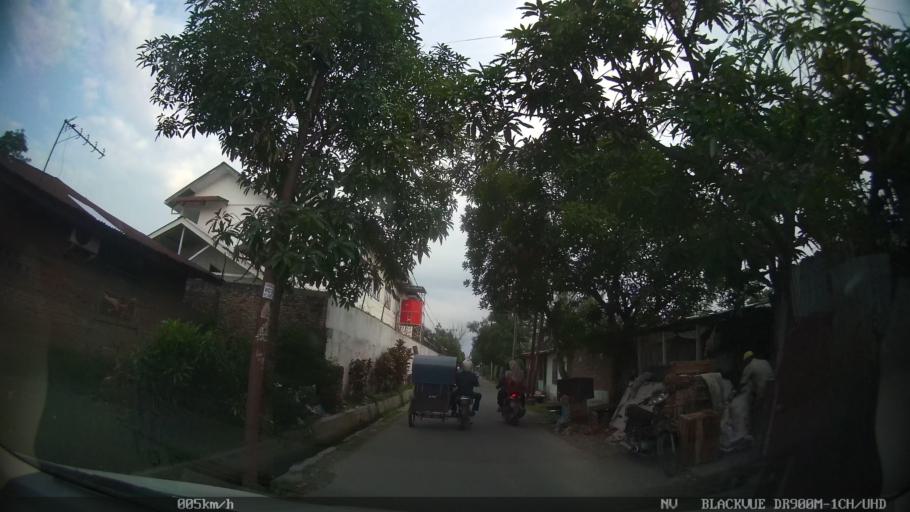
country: ID
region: North Sumatra
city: Medan
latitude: 3.6097
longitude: 98.6849
